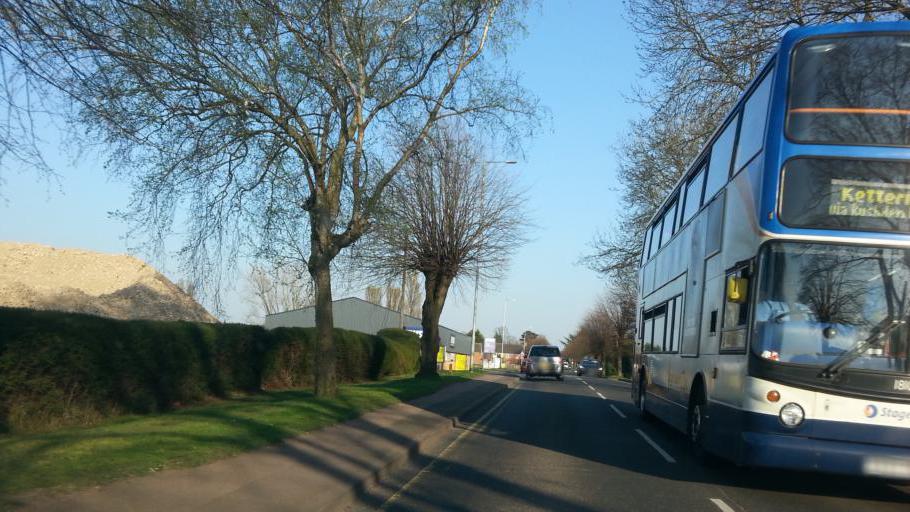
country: GB
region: England
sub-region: Northamptonshire
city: Rushden
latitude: 52.2963
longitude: -0.6226
